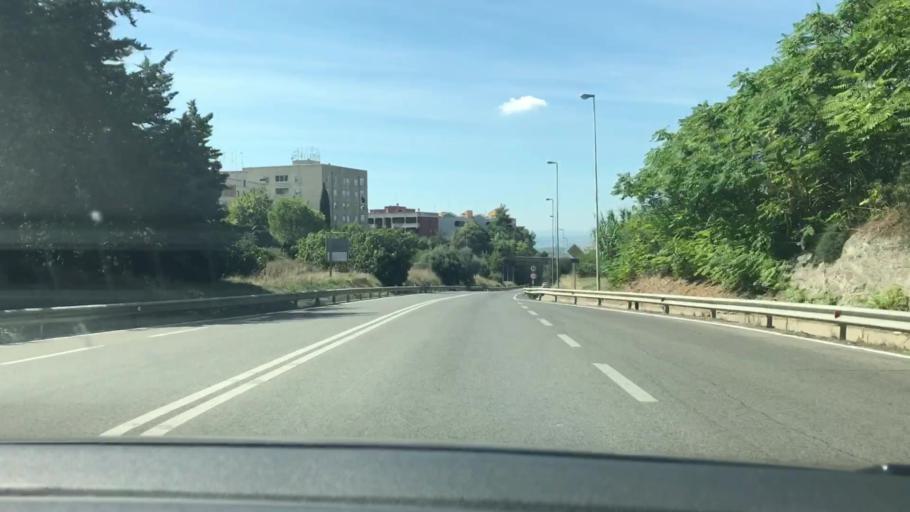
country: IT
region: Basilicate
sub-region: Provincia di Matera
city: Matera
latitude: 40.6786
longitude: 16.5846
